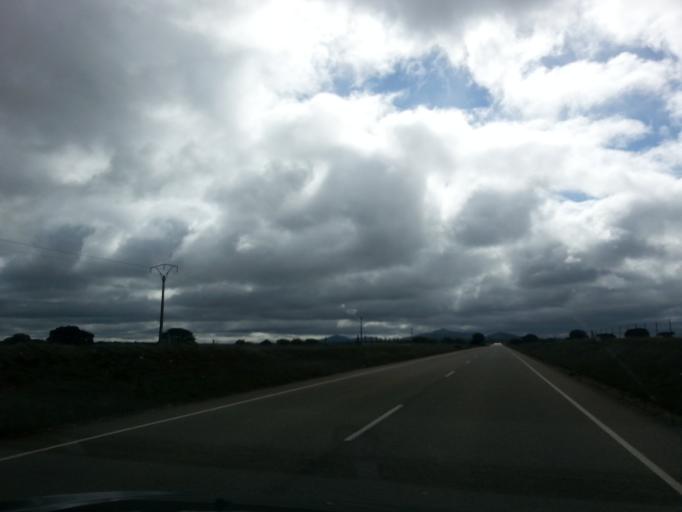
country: ES
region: Castille and Leon
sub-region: Provincia de Salamanca
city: Abusejo
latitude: 40.7023
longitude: -6.1375
